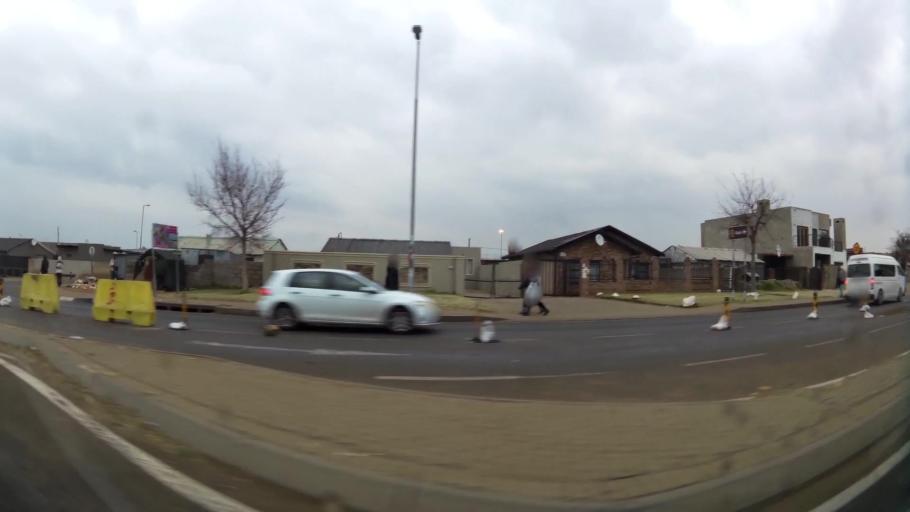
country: ZA
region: Gauteng
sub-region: City of Johannesburg Metropolitan Municipality
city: Soweto
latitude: -26.2518
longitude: 27.8542
